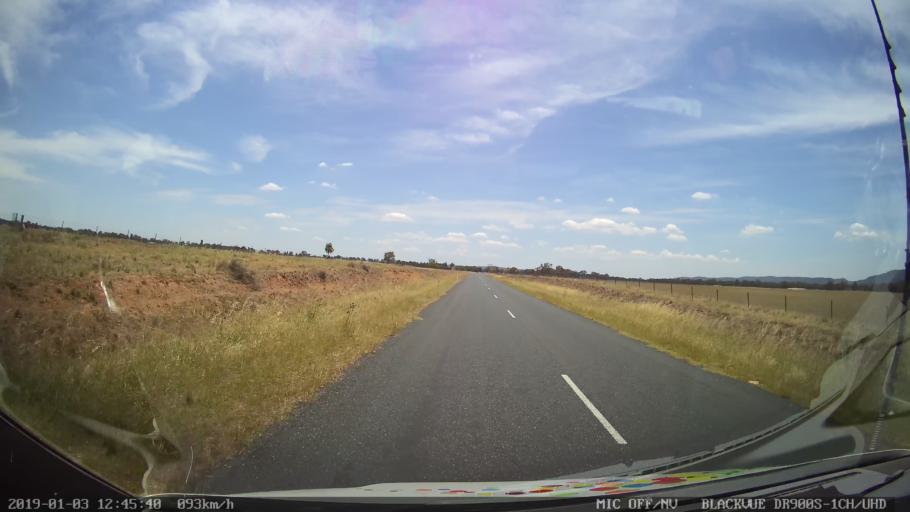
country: AU
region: New South Wales
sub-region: Weddin
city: Grenfell
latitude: -33.7466
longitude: 148.2253
